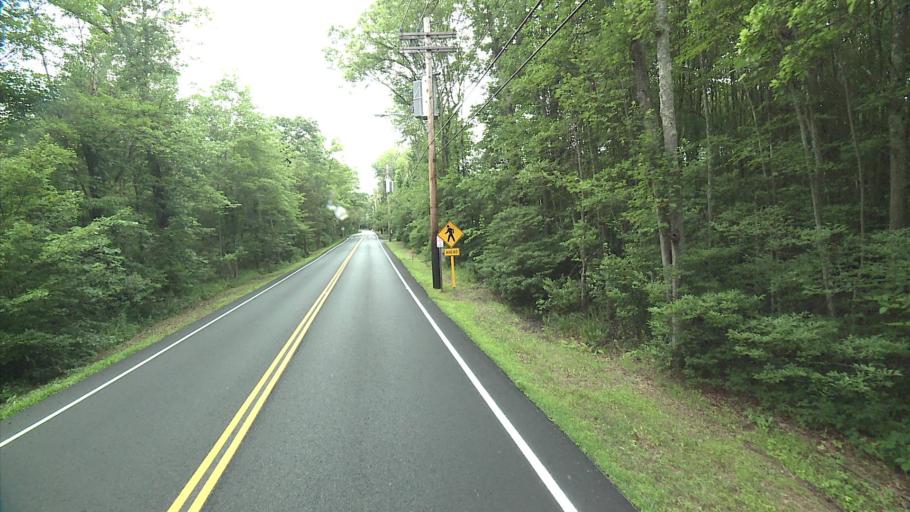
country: US
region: Connecticut
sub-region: New Haven County
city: Wallingford Center
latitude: 41.4121
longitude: -72.7987
